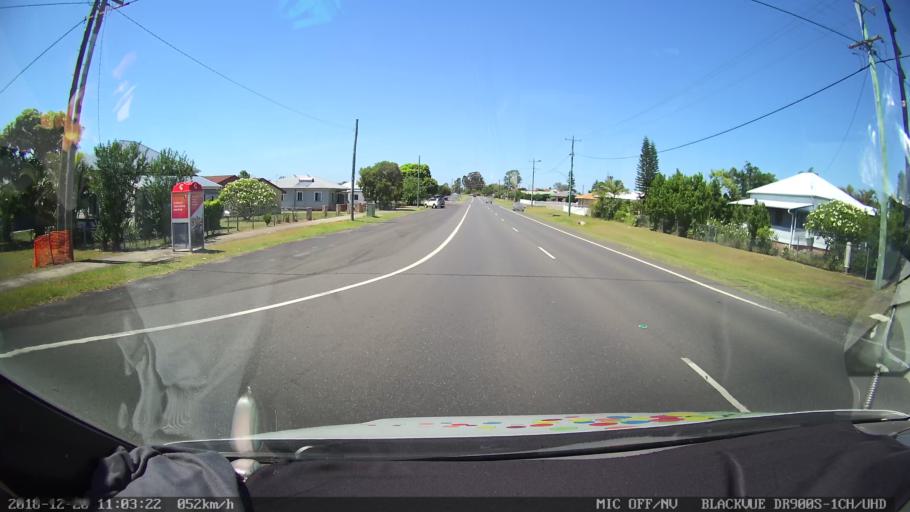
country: AU
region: New South Wales
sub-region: Richmond Valley
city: Casino
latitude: -28.8765
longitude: 153.0432
